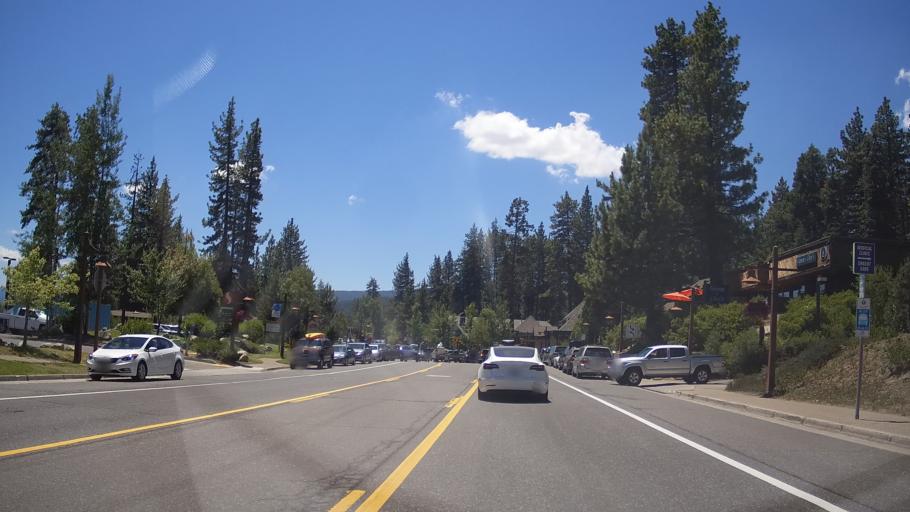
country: US
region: California
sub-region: Placer County
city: Sunnyside-Tahoe City
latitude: 39.1746
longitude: -120.1373
